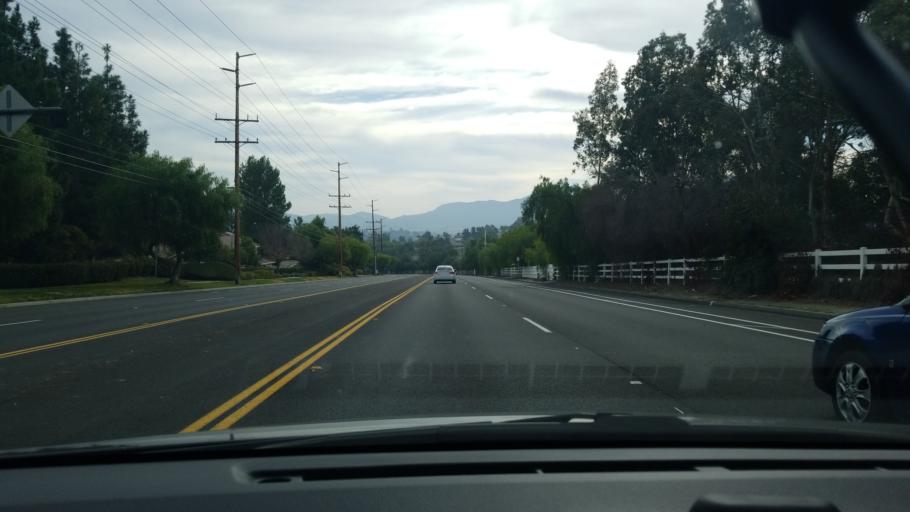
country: US
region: California
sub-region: Riverside County
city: Temecula
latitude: 33.4926
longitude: -117.1112
